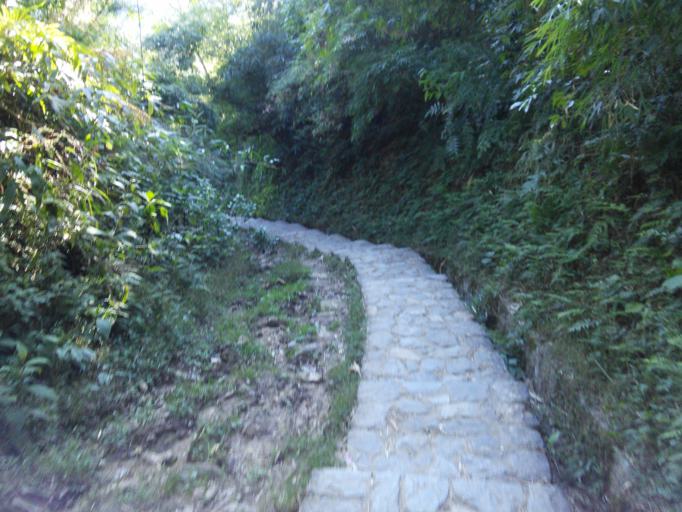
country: VN
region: Lao Cai
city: Sa Pa
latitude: 22.3516
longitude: 103.7735
